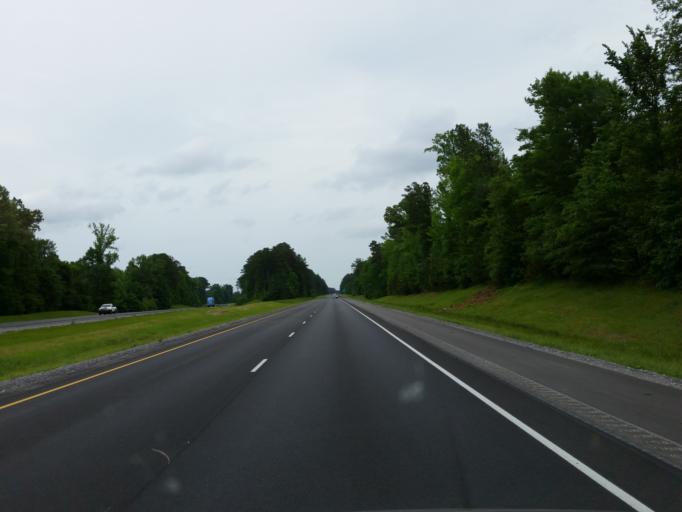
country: US
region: Mississippi
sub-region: Jones County
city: Sharon
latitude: 31.9443
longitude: -88.9860
